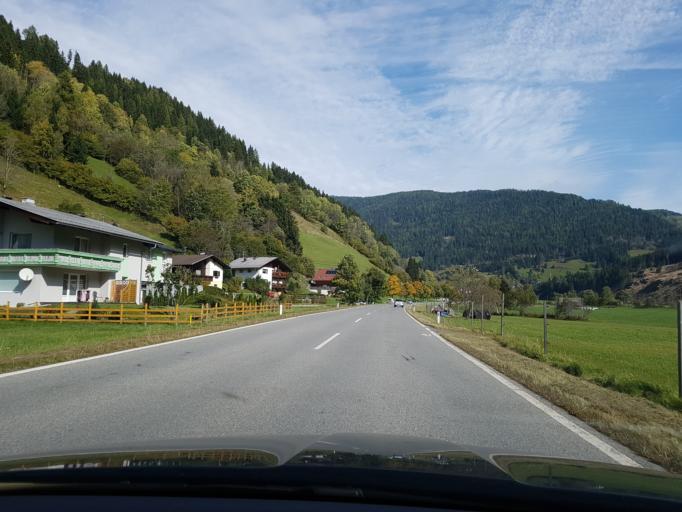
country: AT
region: Carinthia
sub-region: Politischer Bezirk Spittal an der Drau
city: Kleinkirchheim
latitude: 46.8452
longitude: 13.8817
